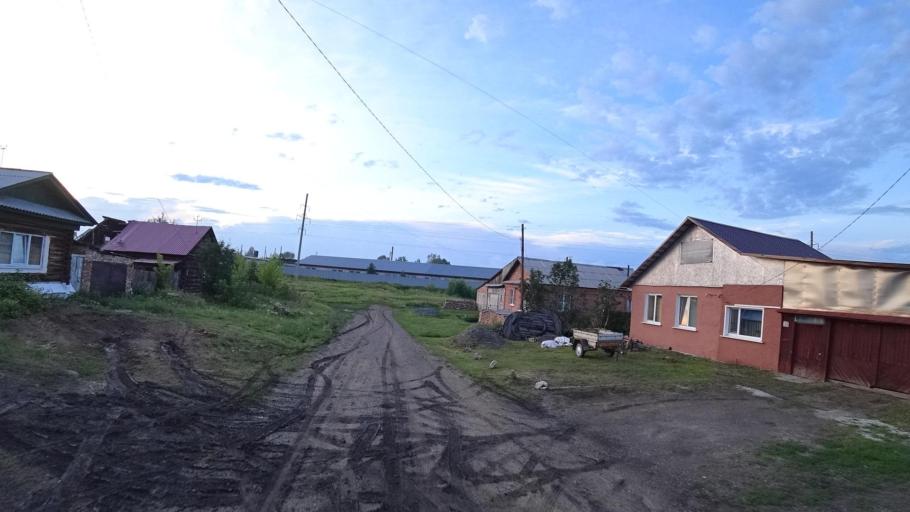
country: RU
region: Sverdlovsk
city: Kamyshlov
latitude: 56.8628
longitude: 62.7130
